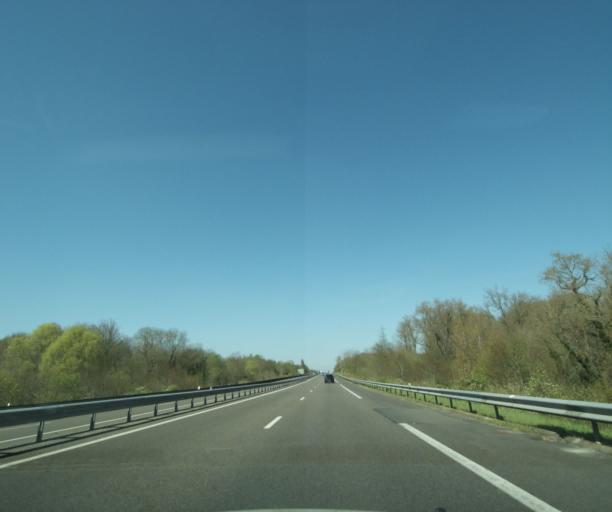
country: FR
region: Bourgogne
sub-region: Departement de la Nievre
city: Cosne-Cours-sur-Loire
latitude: 47.3646
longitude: 2.9234
